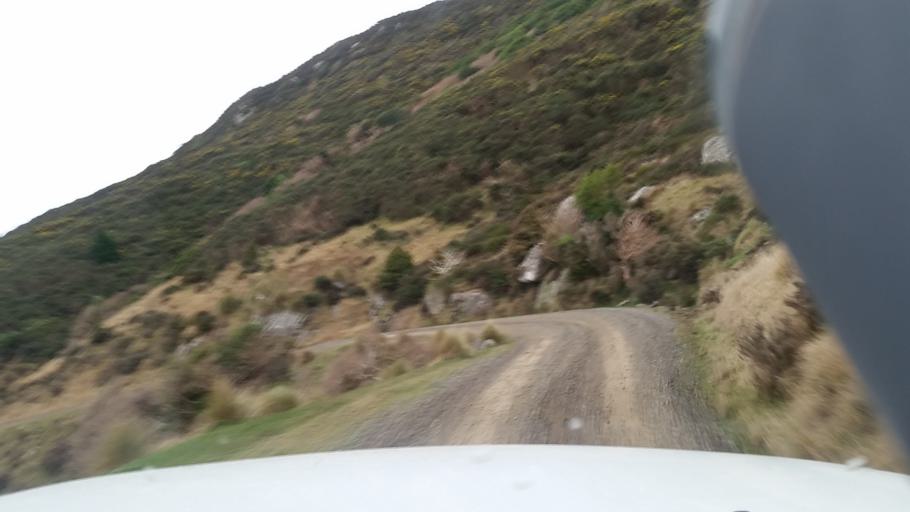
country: NZ
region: Canterbury
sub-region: Christchurch City
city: Christchurch
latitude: -43.8525
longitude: 172.8882
